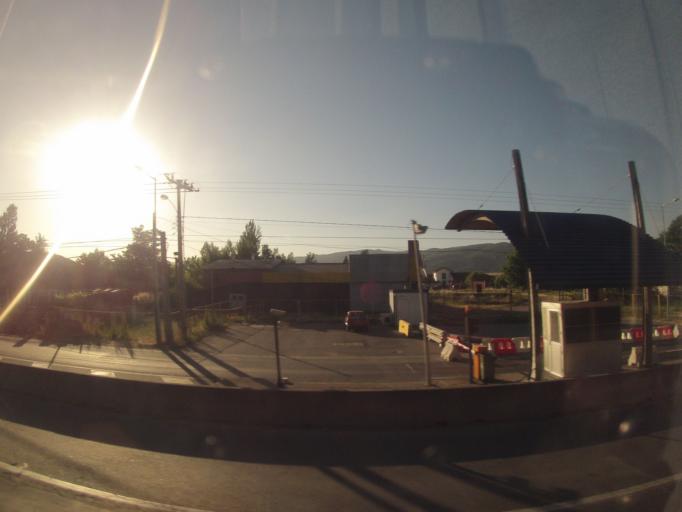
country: CL
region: O'Higgins
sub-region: Provincia de Colchagua
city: Chimbarongo
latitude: -34.7144
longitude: -71.0305
